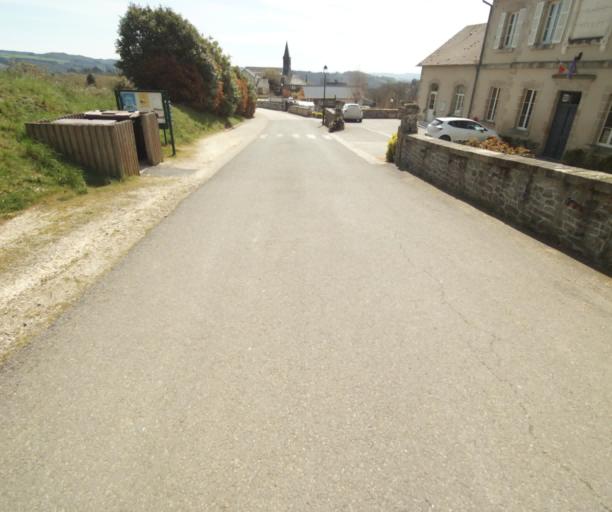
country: FR
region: Limousin
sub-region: Departement de la Correze
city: Naves
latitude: 45.3618
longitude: 1.8005
